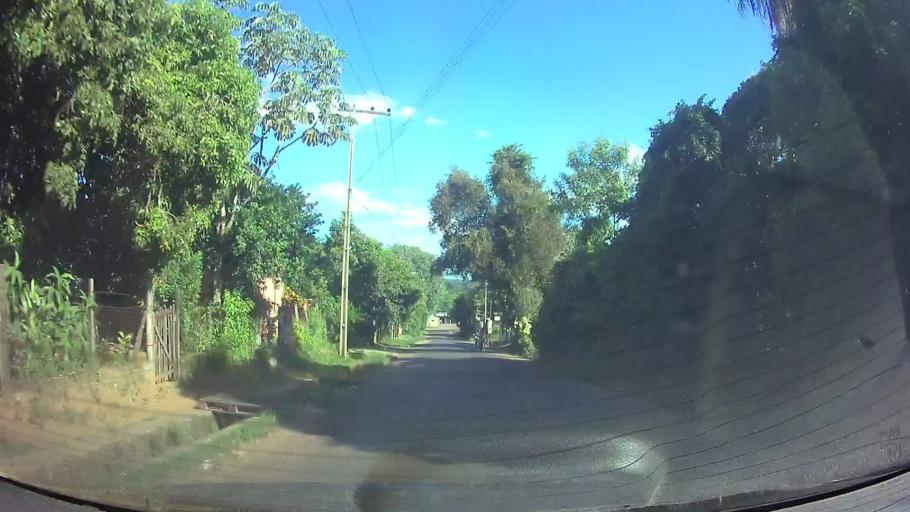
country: PY
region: Cordillera
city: Caacupe
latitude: -25.3772
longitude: -57.1371
